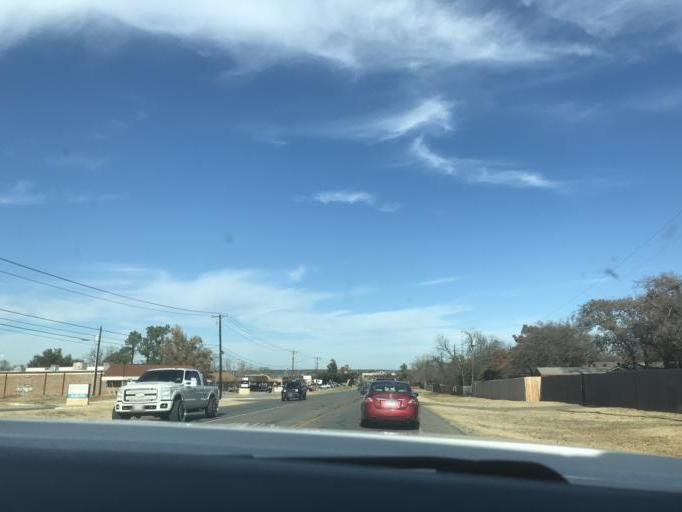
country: US
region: Texas
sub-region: Erath County
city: Stephenville
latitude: 32.2206
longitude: -98.2366
